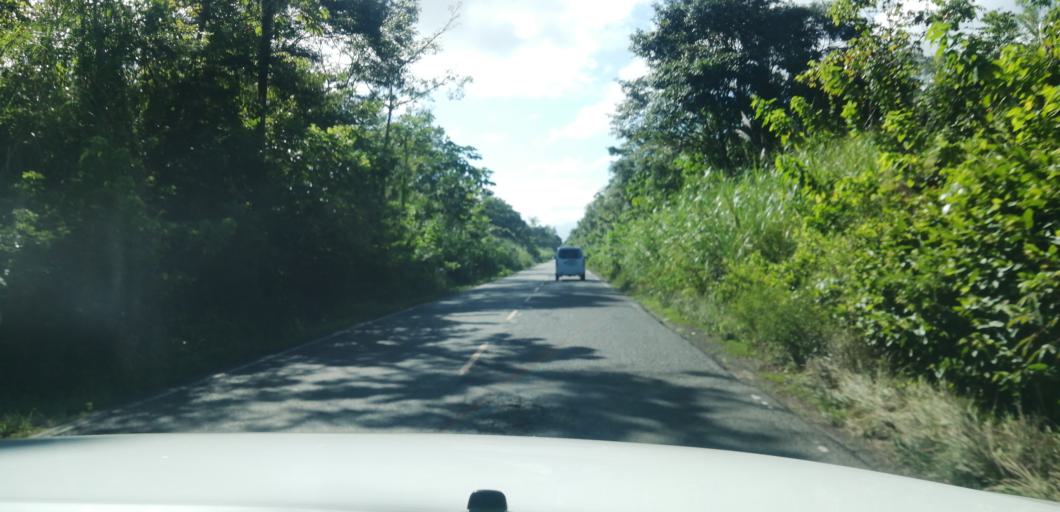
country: PA
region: Panama
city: Canita
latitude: 9.1502
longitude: -78.6936
